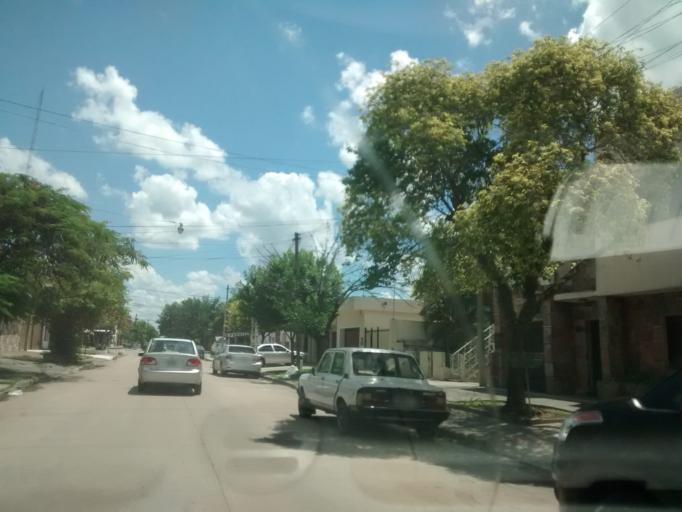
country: AR
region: Chaco
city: Resistencia
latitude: -27.4584
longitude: -58.9911
